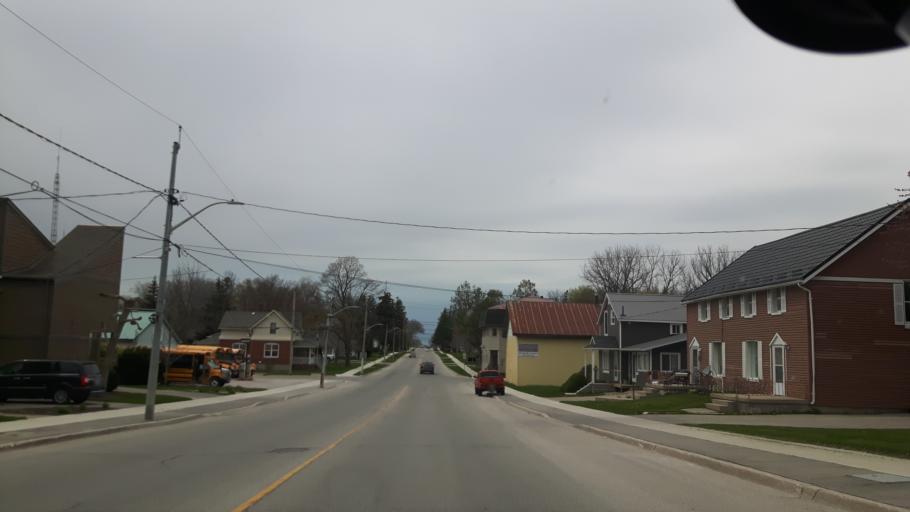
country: CA
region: Ontario
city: Bluewater
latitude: 43.6177
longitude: -81.5410
